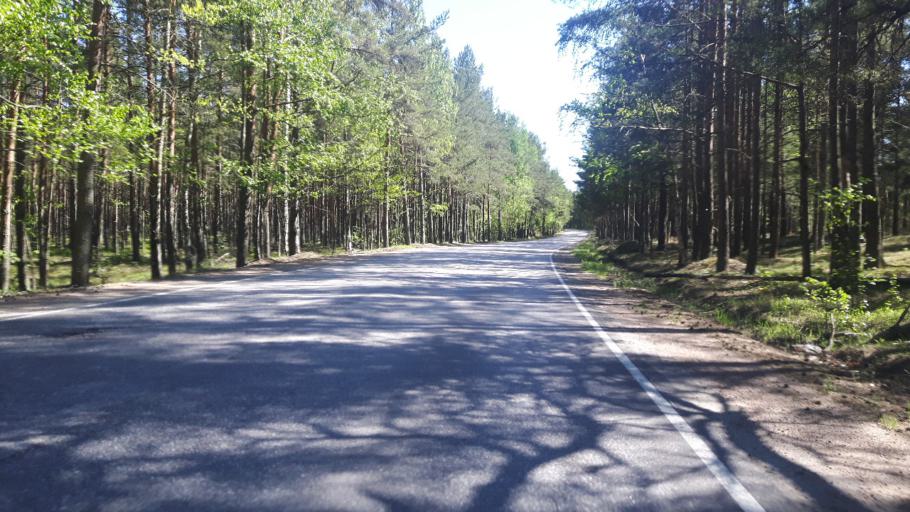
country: RU
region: Leningrad
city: Glebychevo
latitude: 60.2923
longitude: 28.8685
